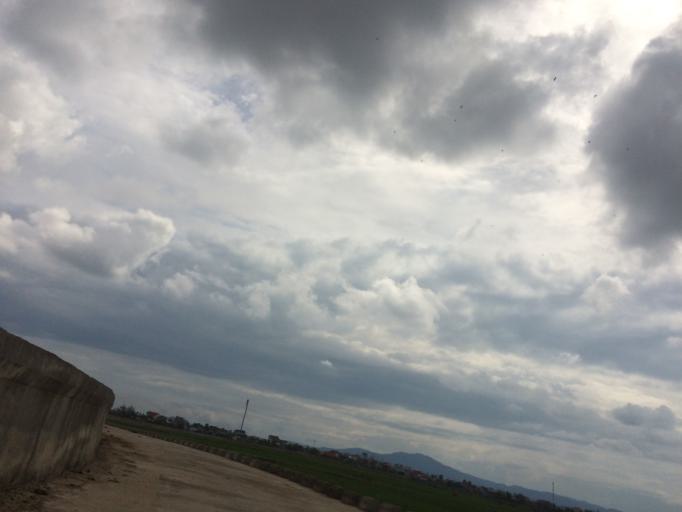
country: VN
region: Ha Tinh
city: Ha Tinh
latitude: 18.3381
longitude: 105.9262
